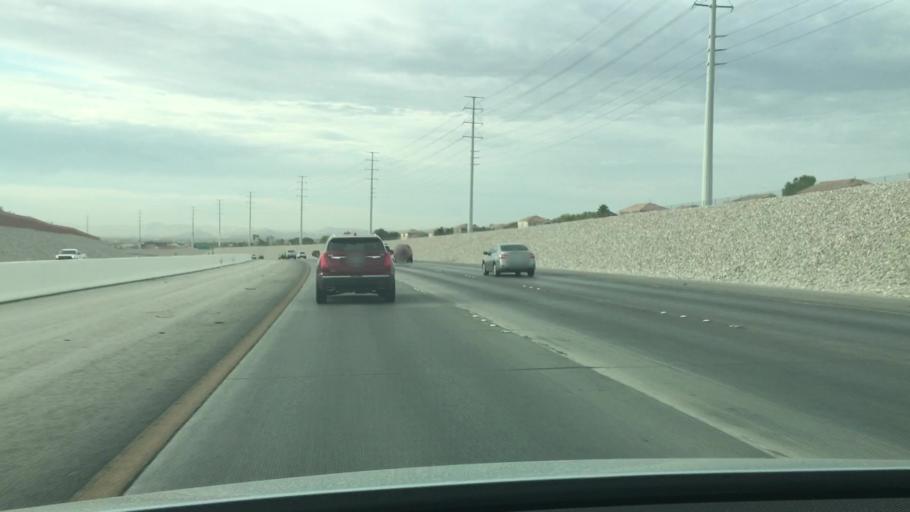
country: US
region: Nevada
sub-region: Clark County
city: Summerlin South
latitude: 36.1288
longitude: -115.3346
